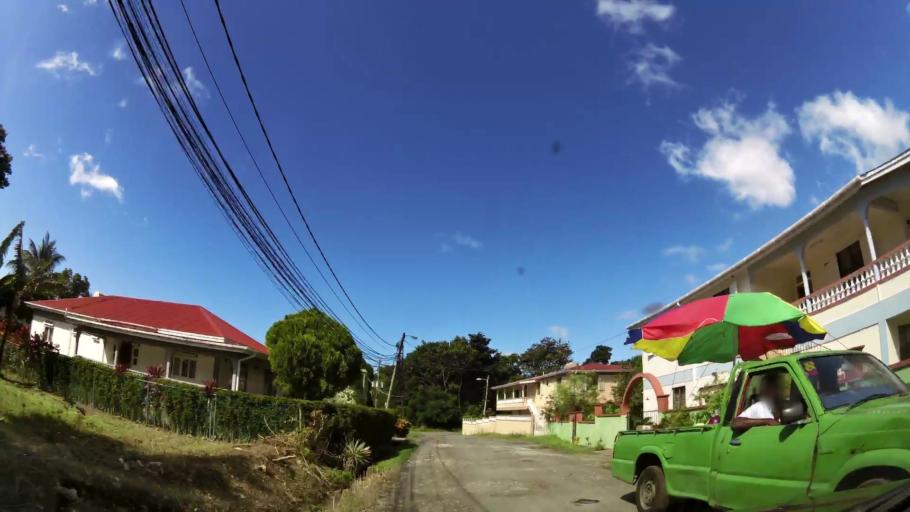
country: DM
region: Saint John
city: Portsmouth
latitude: 15.5594
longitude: -61.4580
